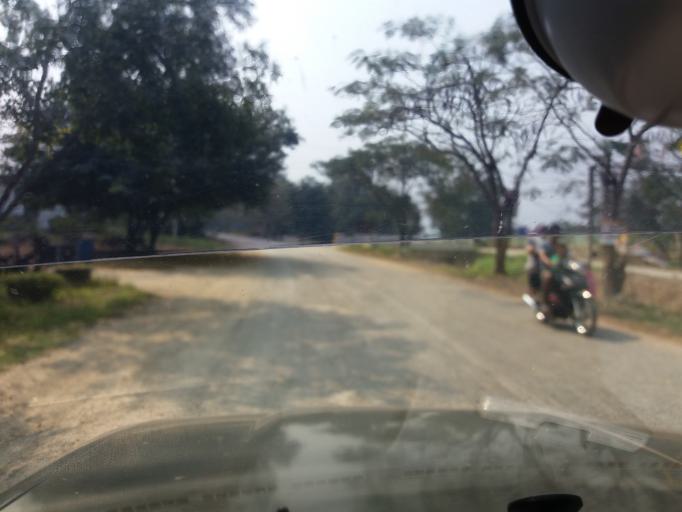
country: TH
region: Suphan Buri
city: Doem Bang Nang Buat
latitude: 14.8945
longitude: 100.2033
